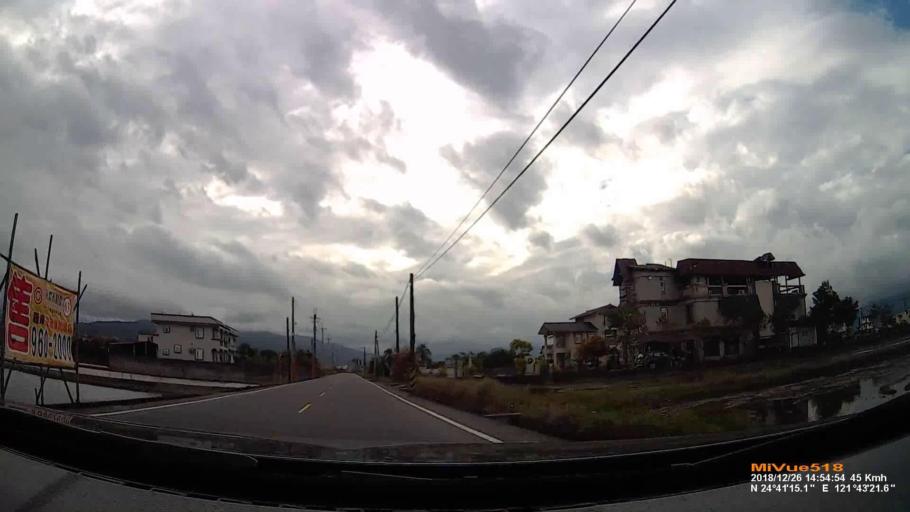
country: TW
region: Taiwan
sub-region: Yilan
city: Yilan
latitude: 24.6875
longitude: 121.7226
